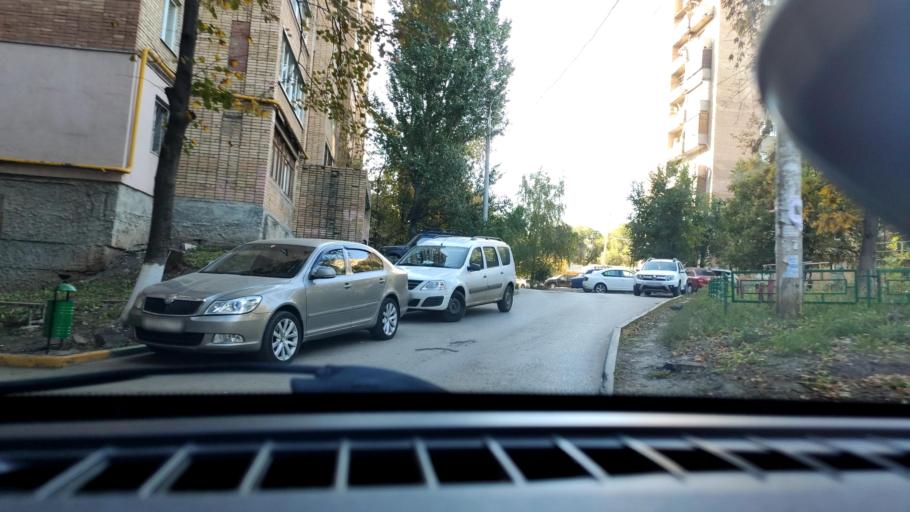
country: RU
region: Samara
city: Samara
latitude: 53.2090
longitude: 50.2225
